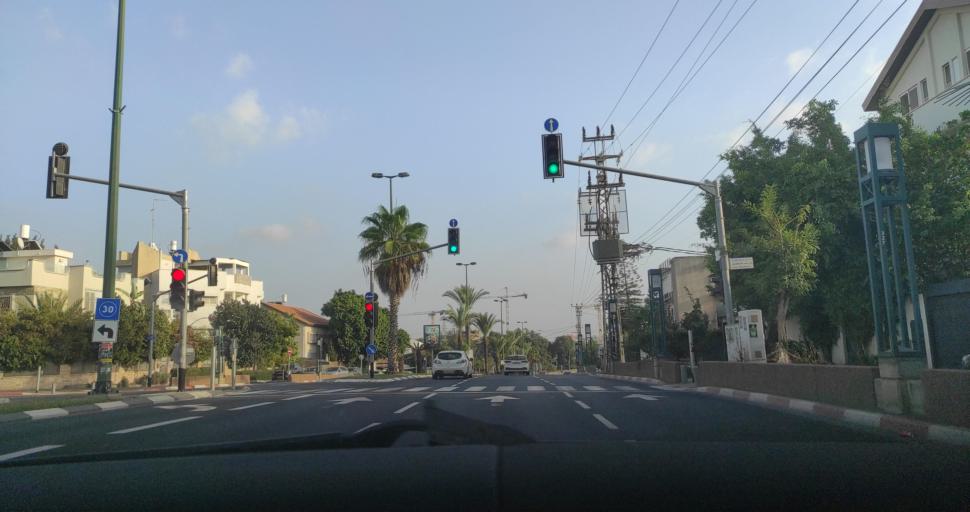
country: IL
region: Tel Aviv
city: Bene Beraq
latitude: 32.1095
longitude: 34.8262
